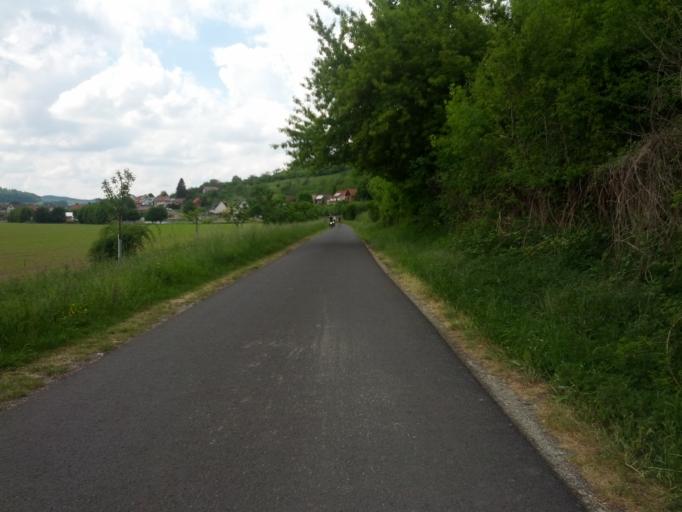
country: DE
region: Thuringia
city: Frankenroda
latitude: 51.1173
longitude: 10.2815
